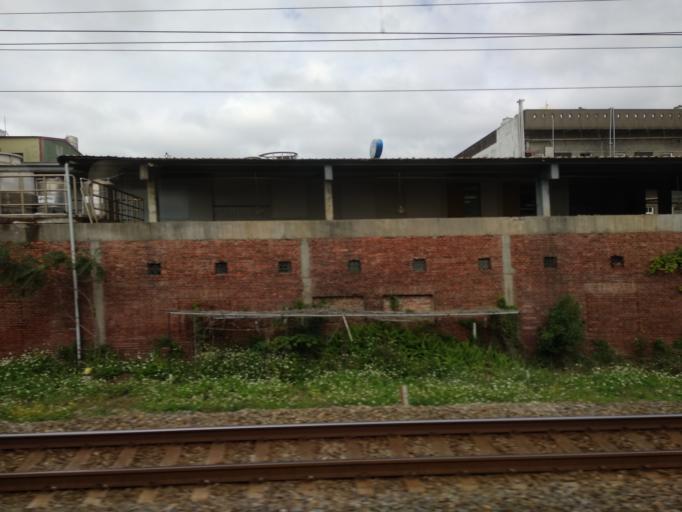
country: TW
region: Taiwan
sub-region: Hsinchu
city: Hsinchu
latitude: 24.8063
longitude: 120.9795
